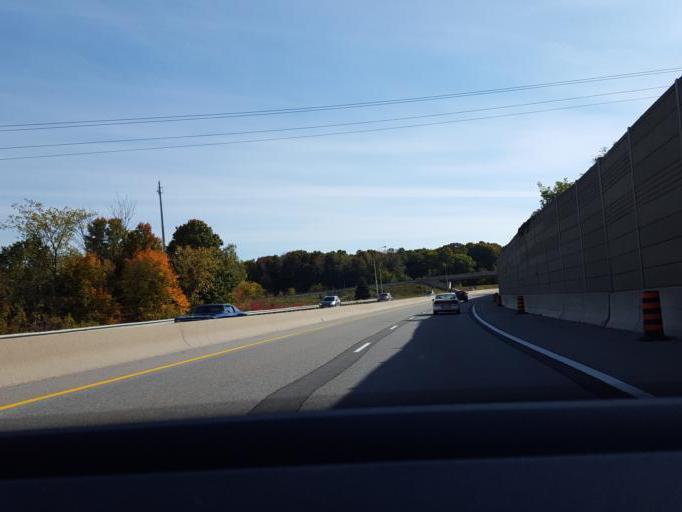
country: CA
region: Ontario
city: Oshawa
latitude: 43.9717
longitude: -78.6101
